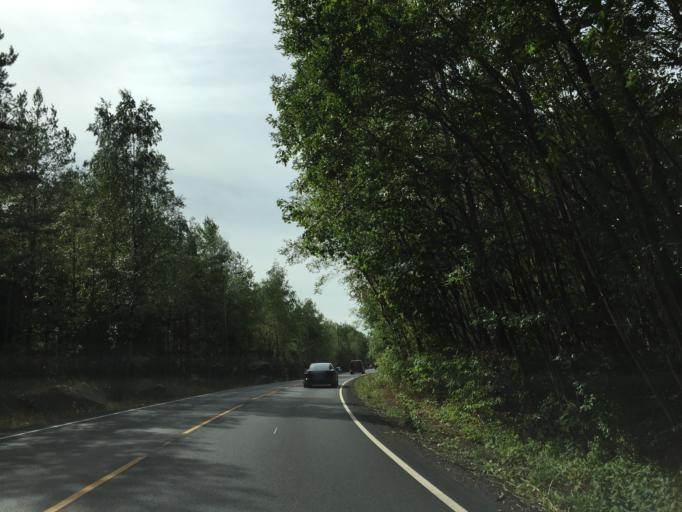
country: NO
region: Ostfold
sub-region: Fredrikstad
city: Fredrikstad
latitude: 59.1415
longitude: 10.9478
